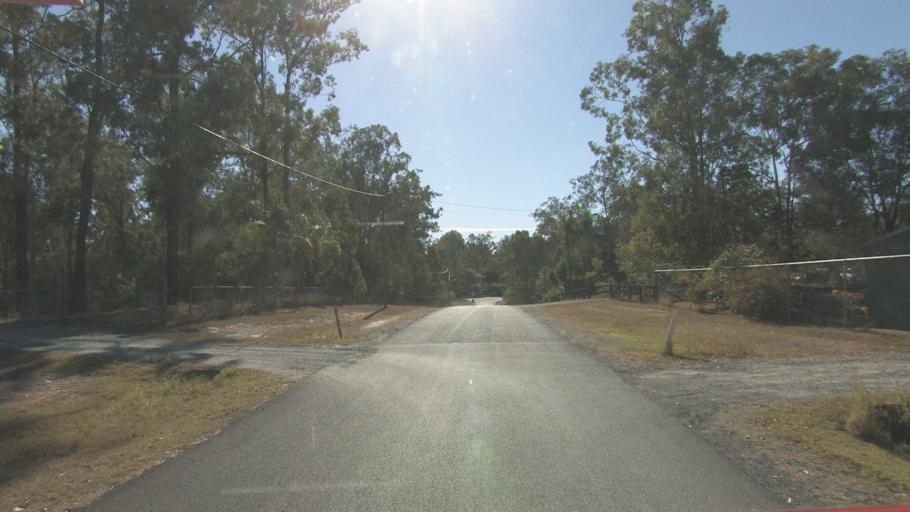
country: AU
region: Queensland
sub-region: Logan
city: North Maclean
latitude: -27.8089
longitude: 152.9671
